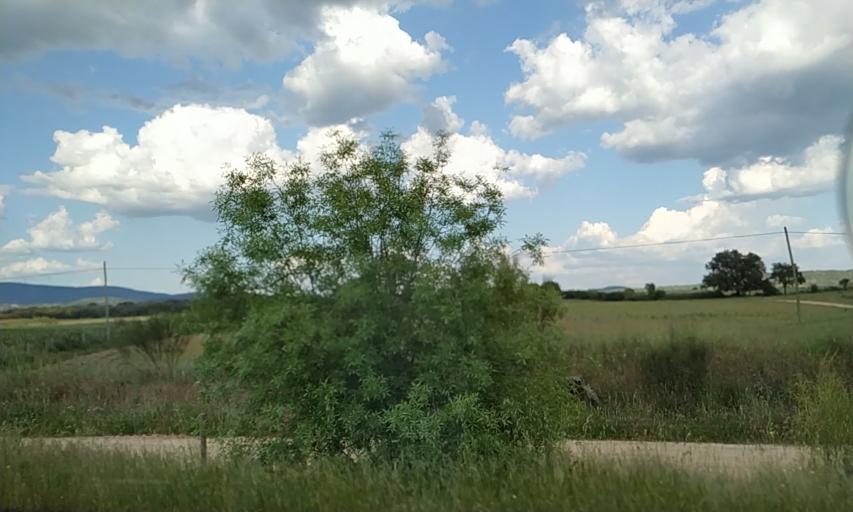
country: PT
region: Portalegre
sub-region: Portalegre
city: Portalegre
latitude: 39.2437
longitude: -7.4503
